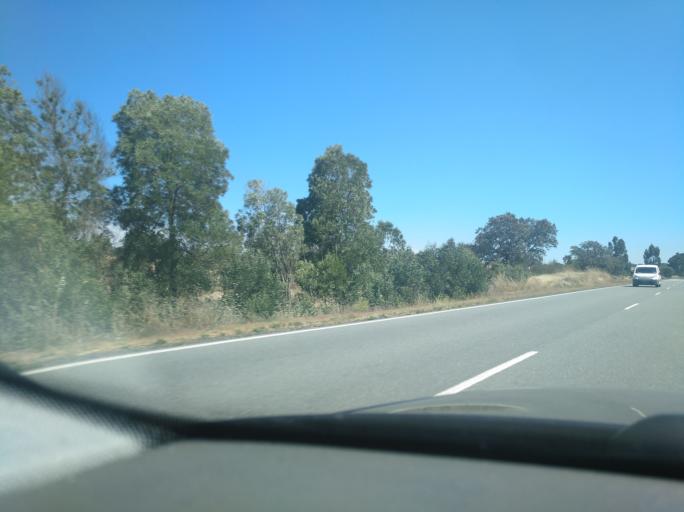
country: PT
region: Beja
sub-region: Castro Verde
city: Castro Verde
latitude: 37.6367
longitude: -8.0819
